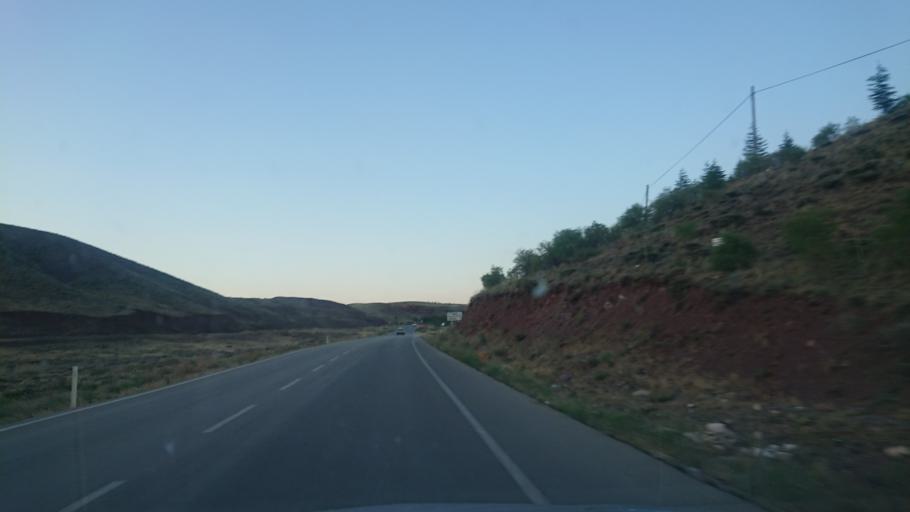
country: TR
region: Aksaray
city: Aksaray
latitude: 38.4211
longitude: 34.0226
